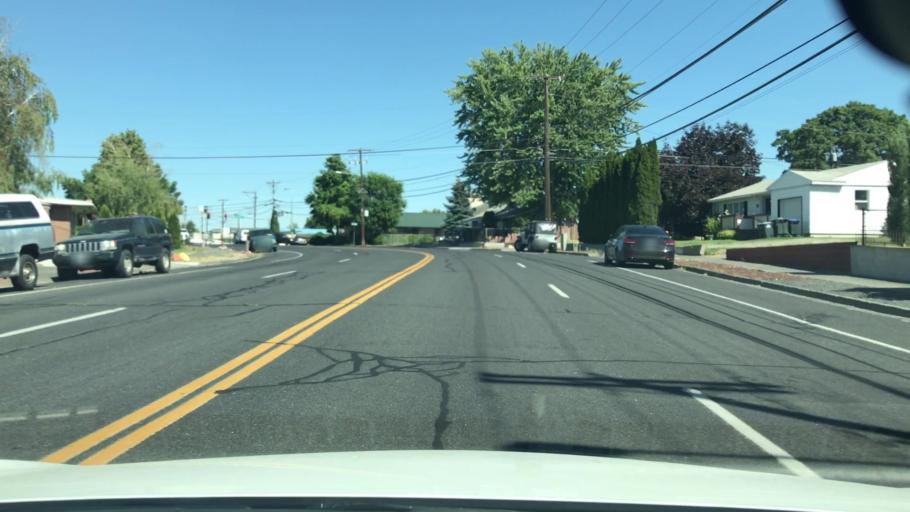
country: US
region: Washington
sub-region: Grant County
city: Moses Lake
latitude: 47.1211
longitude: -119.2699
